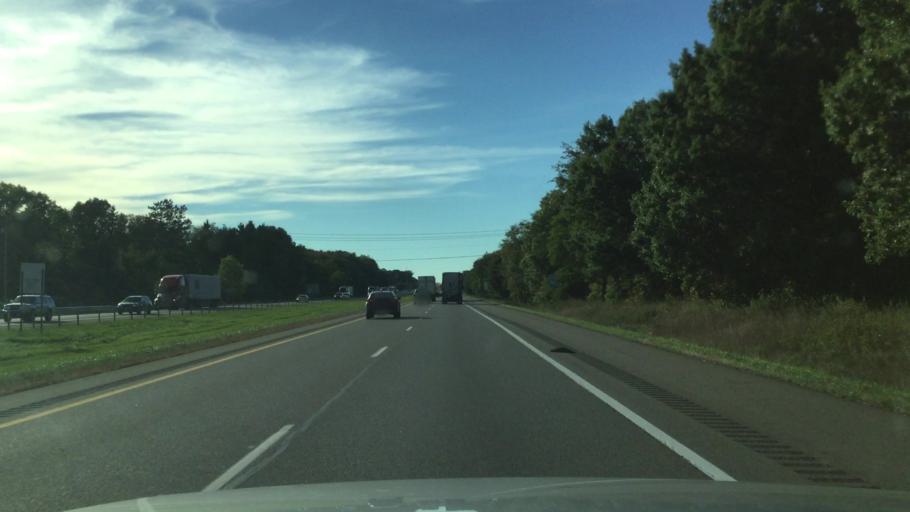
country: US
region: Michigan
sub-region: Calhoun County
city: Lakeview
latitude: 42.2631
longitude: -85.2064
